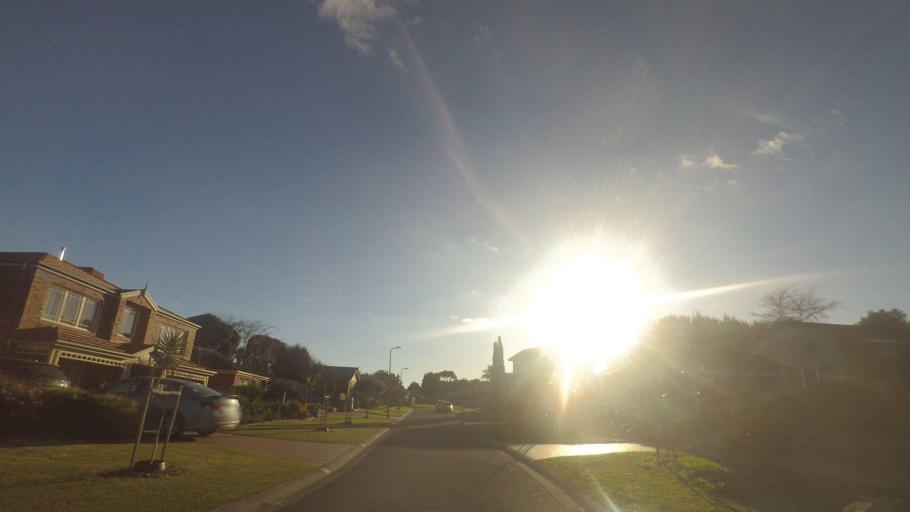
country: AU
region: Victoria
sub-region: Knox
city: Rowville
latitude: -37.9230
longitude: 145.2637
